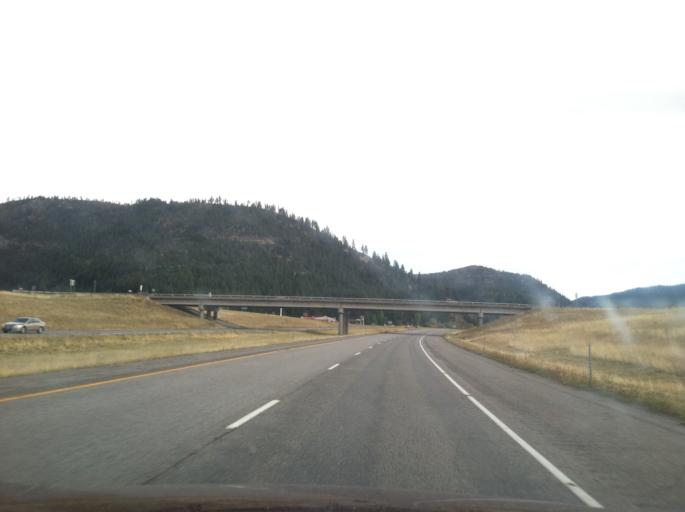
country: US
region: Montana
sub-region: Missoula County
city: Clinton
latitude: 46.7821
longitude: -113.7147
